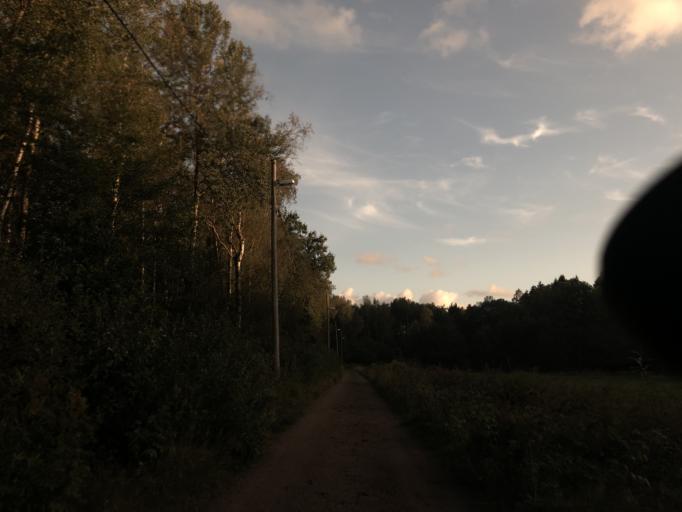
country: SE
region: Vaestra Goetaland
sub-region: Goteborg
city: Majorna
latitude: 57.7636
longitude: 11.9115
